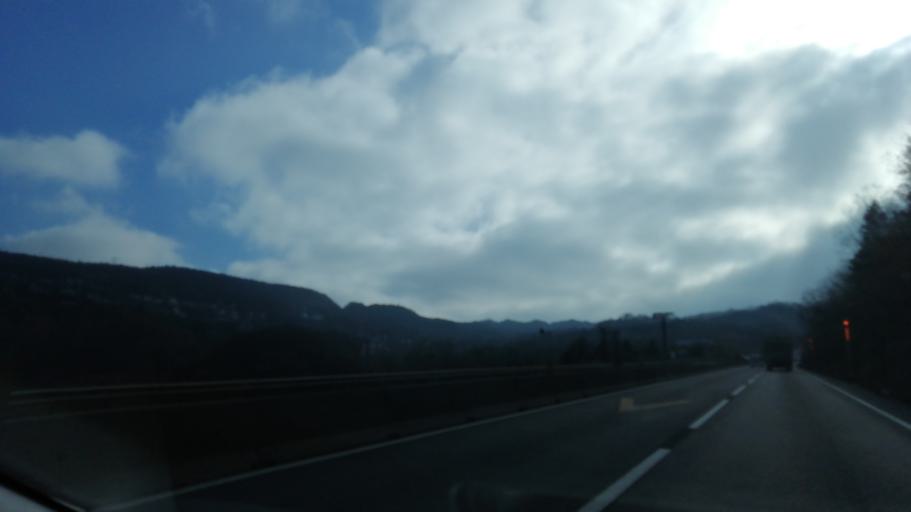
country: TR
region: Duzce
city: Kaynasli
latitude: 40.7532
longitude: 31.3736
